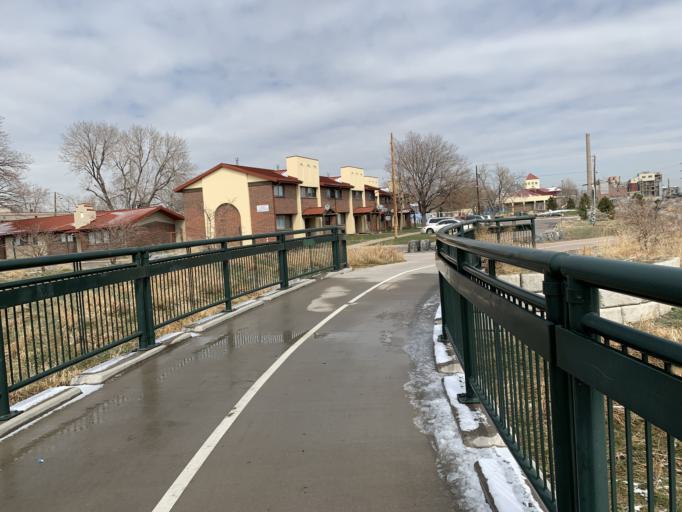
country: US
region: Colorado
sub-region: Denver County
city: Denver
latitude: 39.7310
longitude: -105.0176
